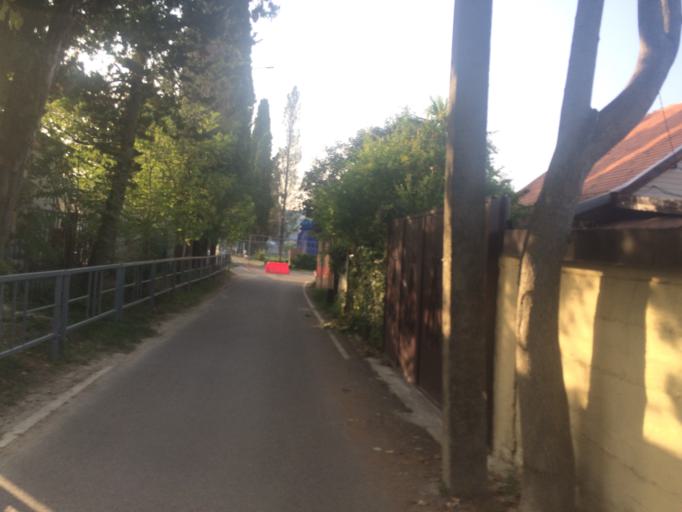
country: RU
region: Krasnodarskiy
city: Adler
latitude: 43.3883
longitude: 39.9864
